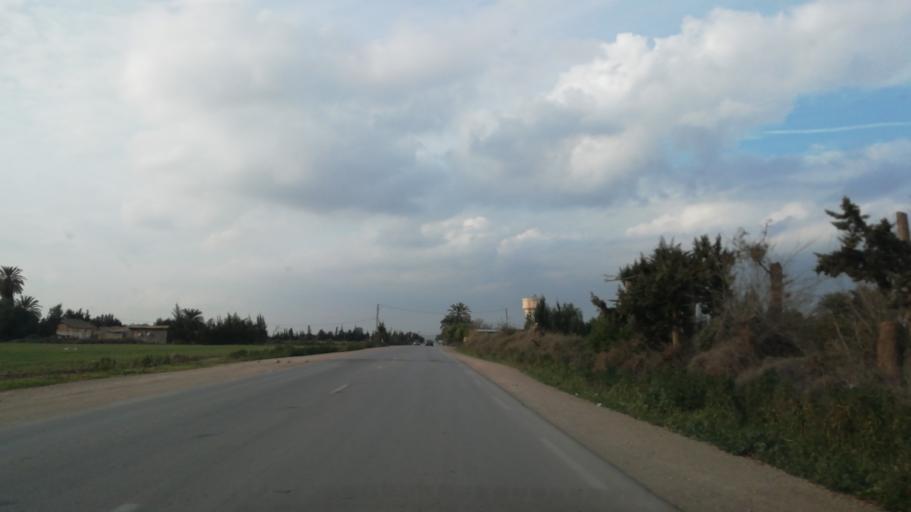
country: DZ
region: Mascara
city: Sig
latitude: 35.6862
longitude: -0.0145
